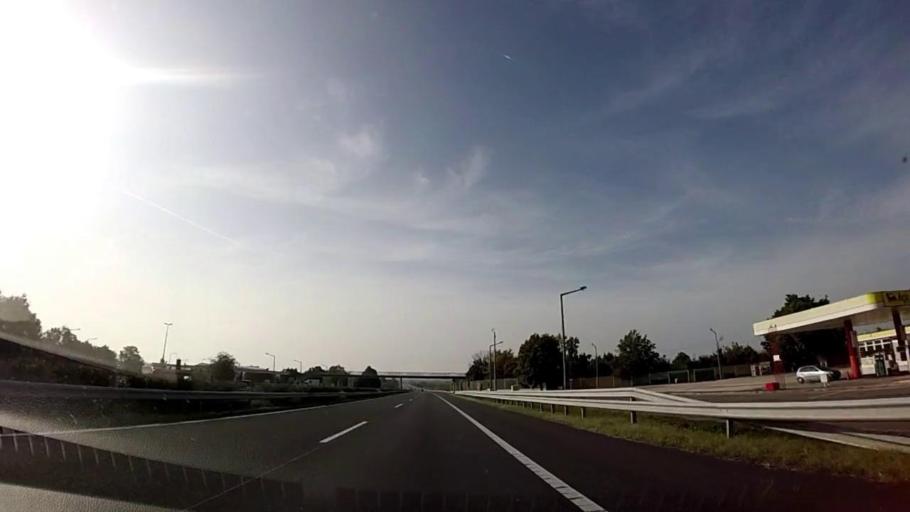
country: HU
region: Somogy
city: Balatonszabadi
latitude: 46.9556
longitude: 18.1545
